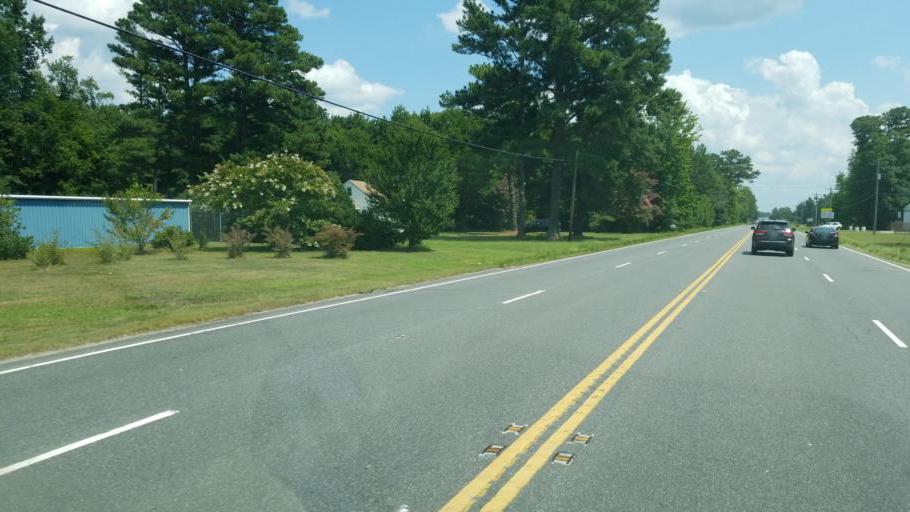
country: US
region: Virginia
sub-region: Isle of Wight County
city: Windsor
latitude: 36.8192
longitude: -76.7606
